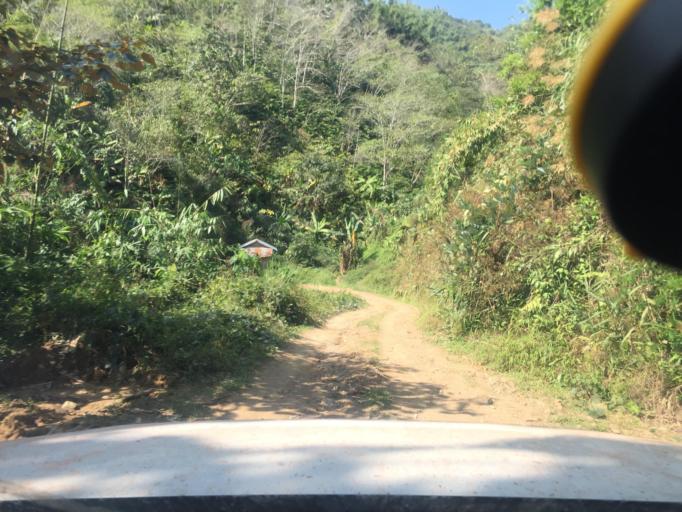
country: LA
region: Phongsali
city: Phongsali
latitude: 21.6570
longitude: 102.4150
